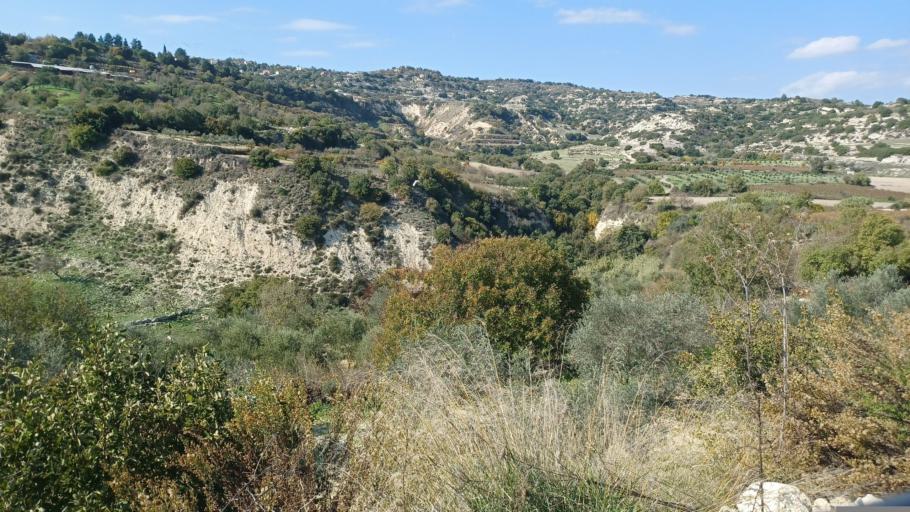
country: CY
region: Pafos
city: Mesogi
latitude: 34.8471
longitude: 32.5127
